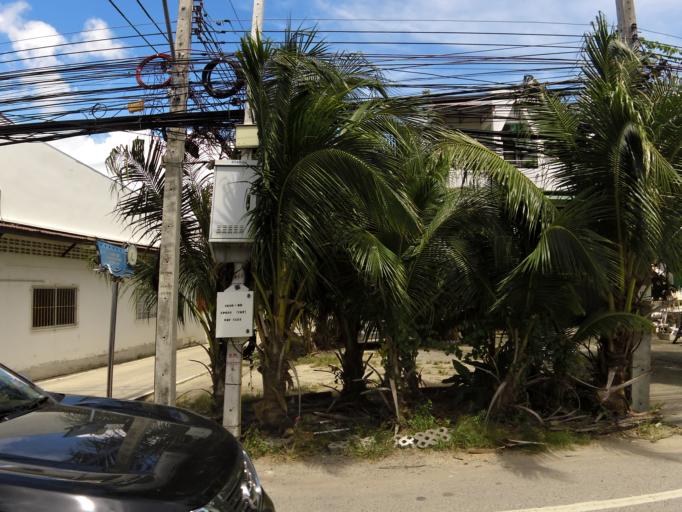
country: TH
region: Phuket
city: Ban Chalong
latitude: 7.8278
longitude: 98.3405
